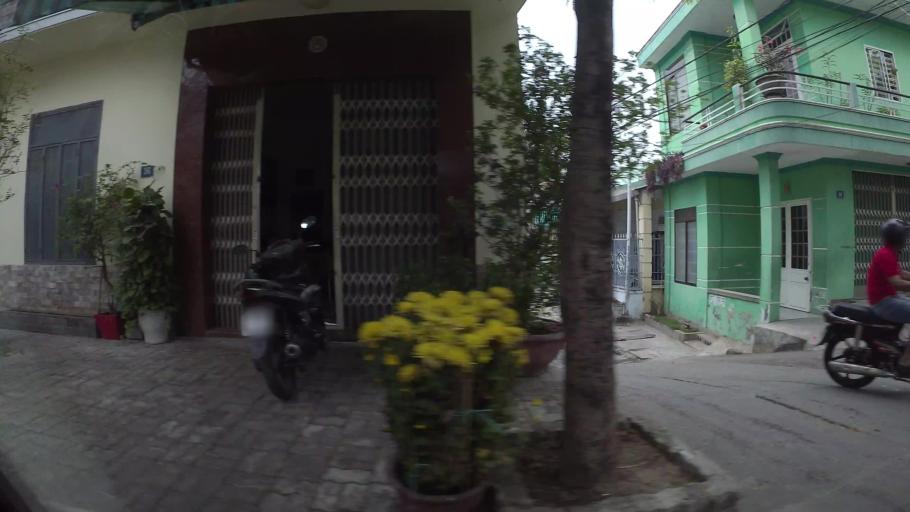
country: VN
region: Da Nang
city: Thanh Khe
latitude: 16.0554
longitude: 108.1843
